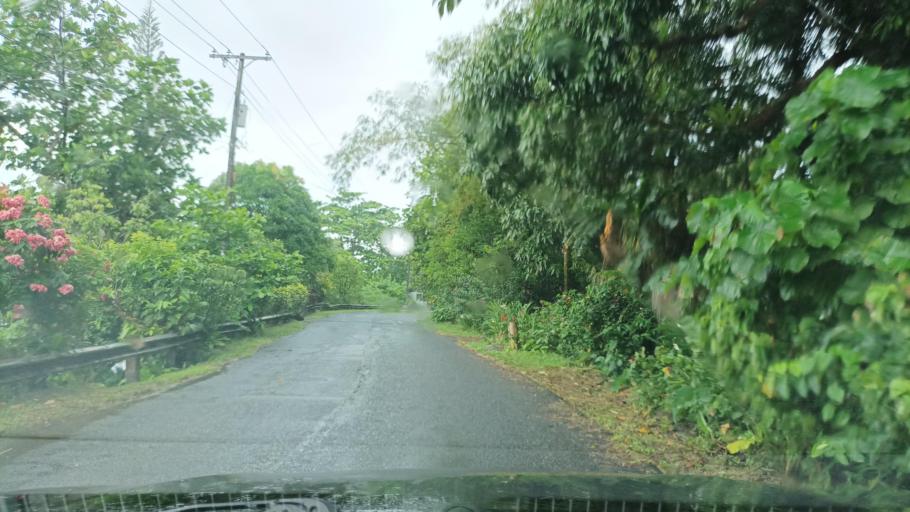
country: FM
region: Pohnpei
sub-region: Kolonia Municipality
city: Kolonia
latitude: 6.9615
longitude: 158.2494
